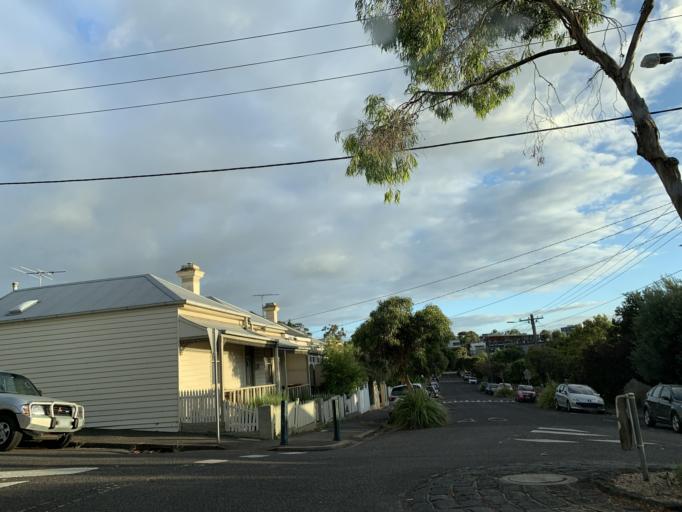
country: AU
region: Victoria
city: Kensington
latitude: -37.7848
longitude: 144.9338
